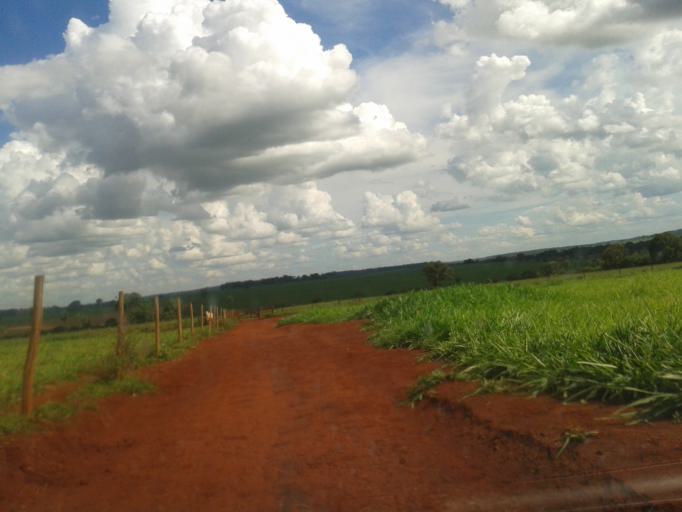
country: BR
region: Minas Gerais
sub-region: Capinopolis
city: Capinopolis
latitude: -18.7792
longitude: -49.8256
